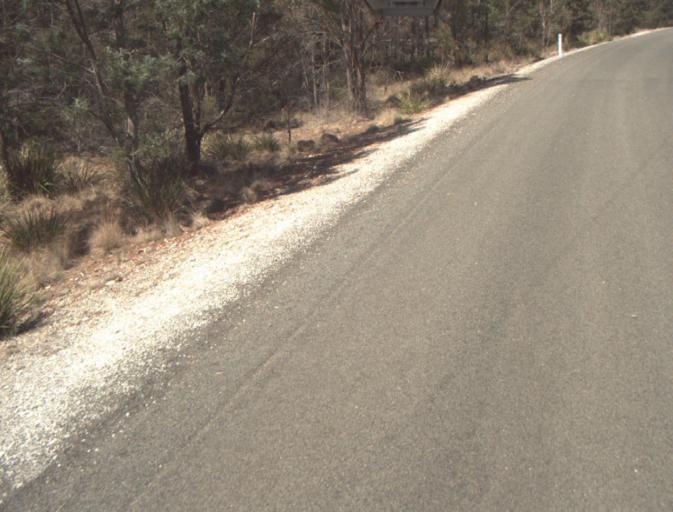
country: AU
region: Tasmania
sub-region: Launceston
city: Mayfield
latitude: -41.3221
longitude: 147.1233
